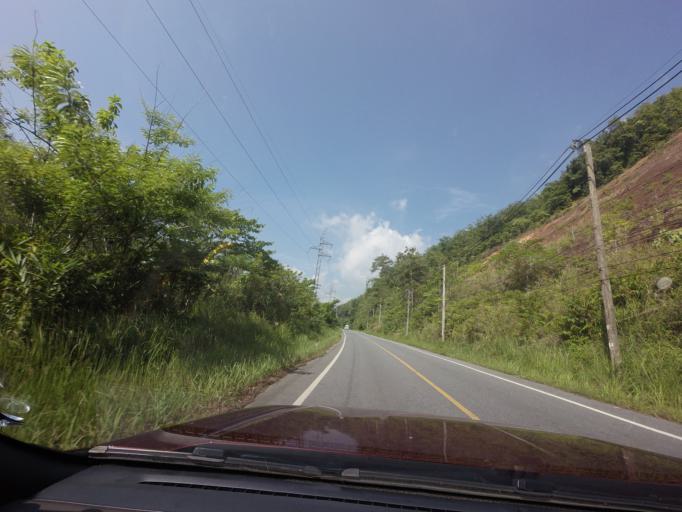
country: TH
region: Yala
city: Betong
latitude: 5.9490
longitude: 101.1909
